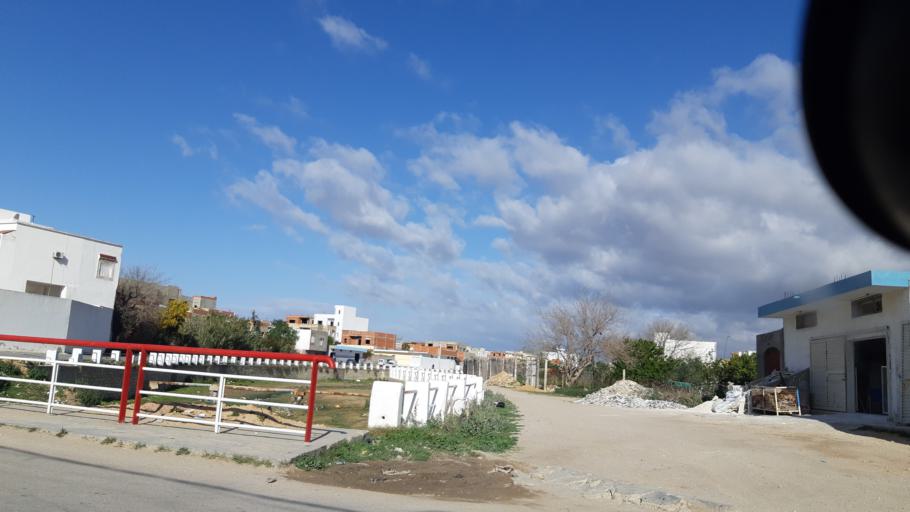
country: TN
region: Susah
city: Akouda
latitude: 35.8718
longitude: 10.5458
